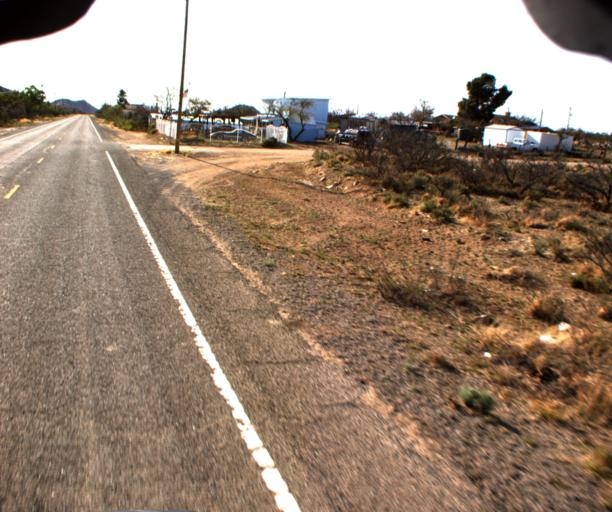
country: US
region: Arizona
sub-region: Cochise County
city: Willcox
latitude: 32.1749
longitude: -109.6128
